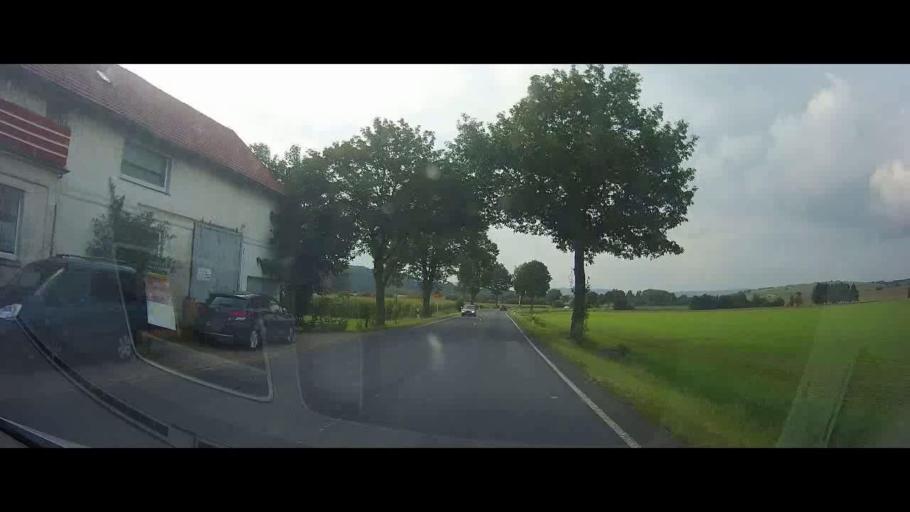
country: DE
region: Lower Saxony
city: Adelebsen
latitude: 51.5890
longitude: 9.6855
